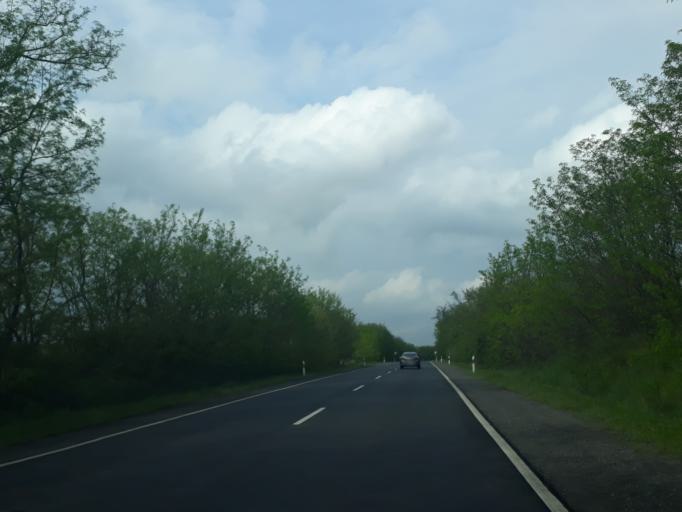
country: HU
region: Szabolcs-Szatmar-Bereg
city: Nyirtass
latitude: 48.1380
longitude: 22.0203
